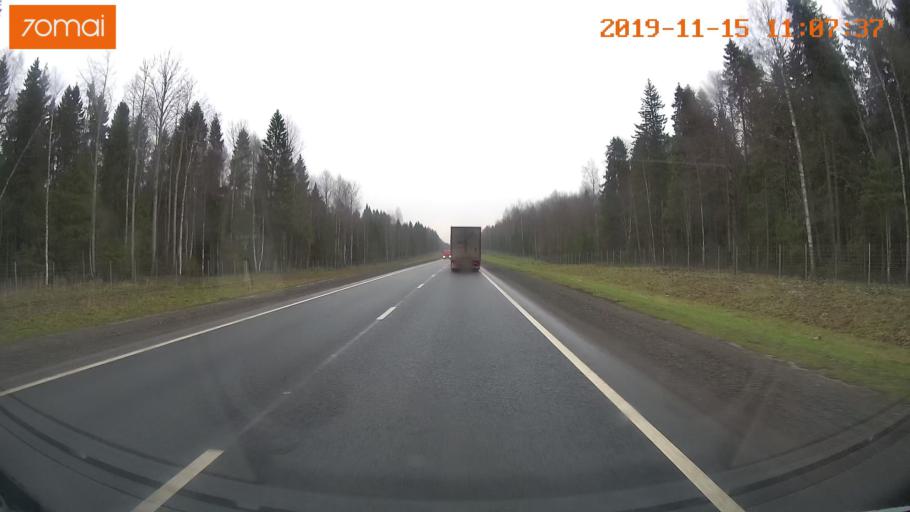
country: RU
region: Vologda
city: Chebsara
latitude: 59.1196
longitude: 39.0542
